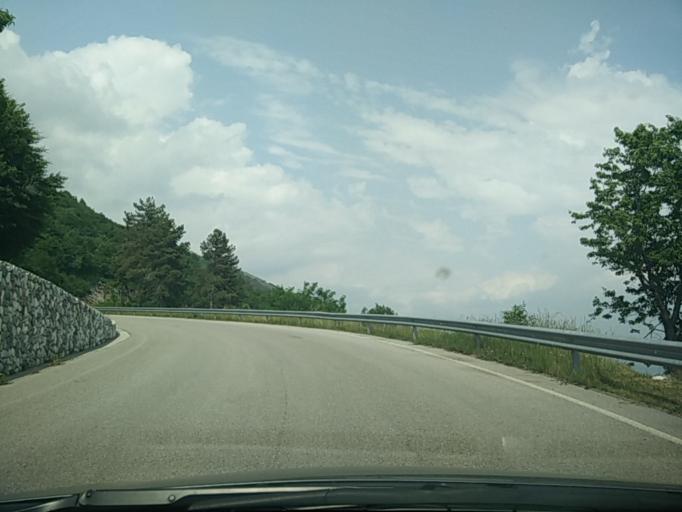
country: IT
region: Friuli Venezia Giulia
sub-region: Provincia di Pordenone
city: Budoia
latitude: 46.0778
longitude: 12.5383
